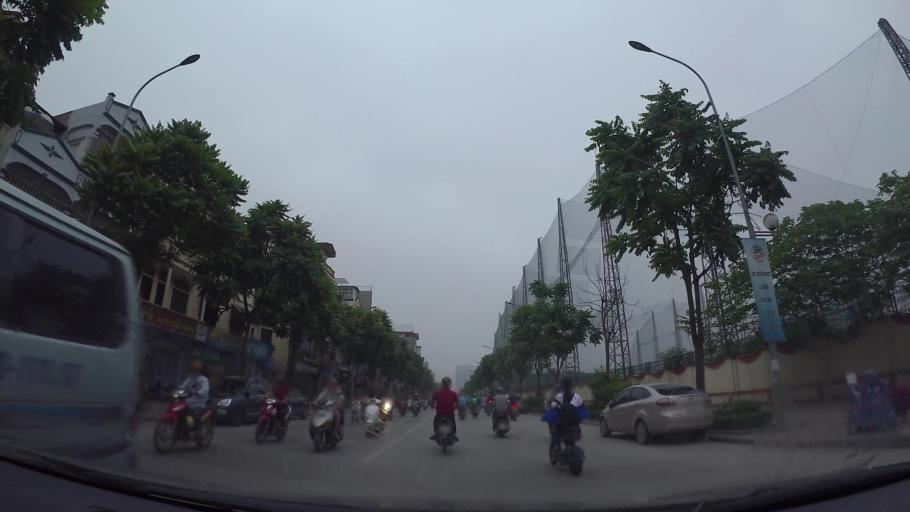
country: VN
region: Ha Noi
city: Hai BaTrung
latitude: 20.9894
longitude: 105.8343
